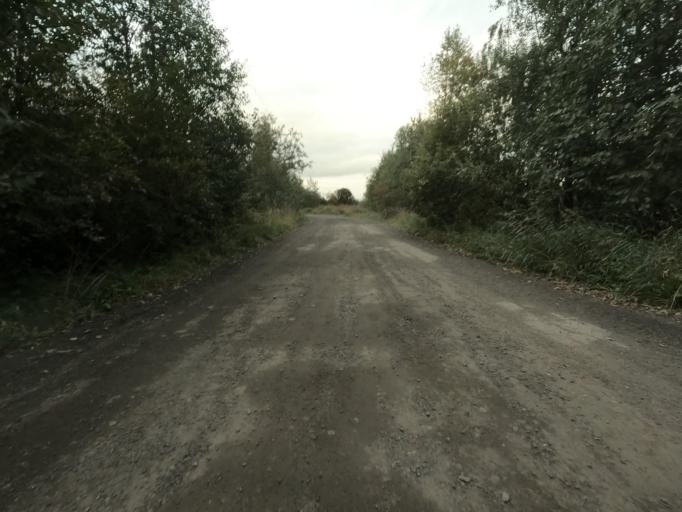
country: RU
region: St.-Petersburg
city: Sapernyy
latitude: 59.7656
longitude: 30.6419
